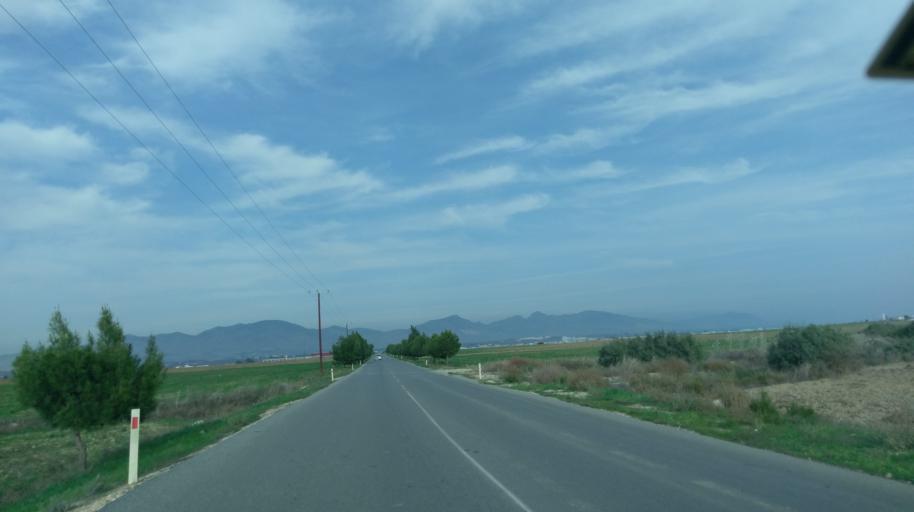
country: CY
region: Lefkosia
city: Mammari
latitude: 35.1987
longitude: 33.2675
